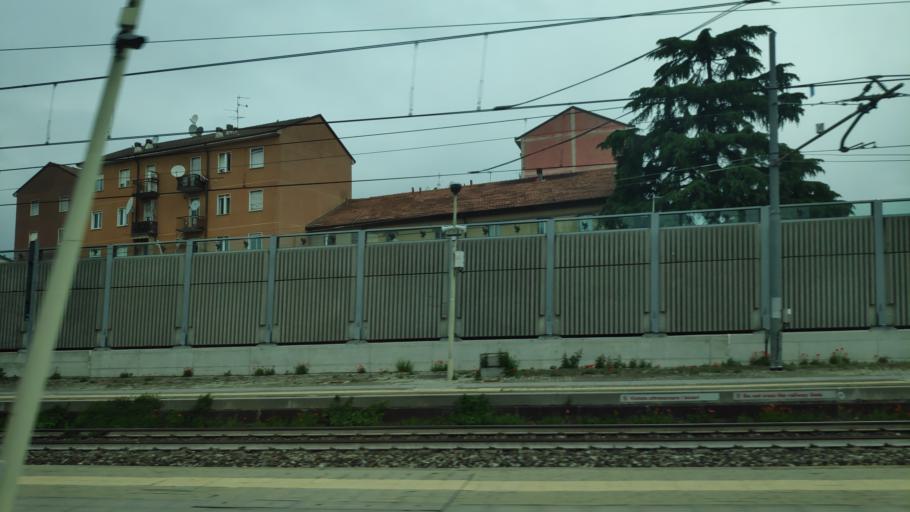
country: IT
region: Lombardy
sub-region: Citta metropolitana di Milano
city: Millepini
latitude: 45.4861
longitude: 9.3301
